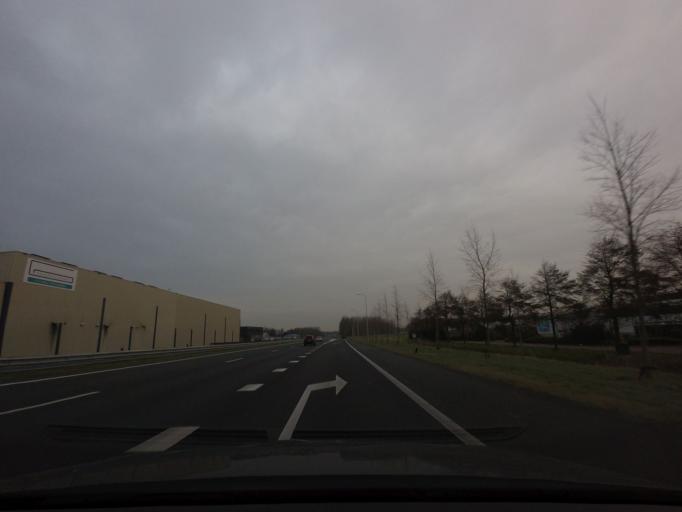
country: NL
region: North Holland
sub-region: Gemeente Medemblik
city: Opperdoes
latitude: 52.8374
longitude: 5.0208
